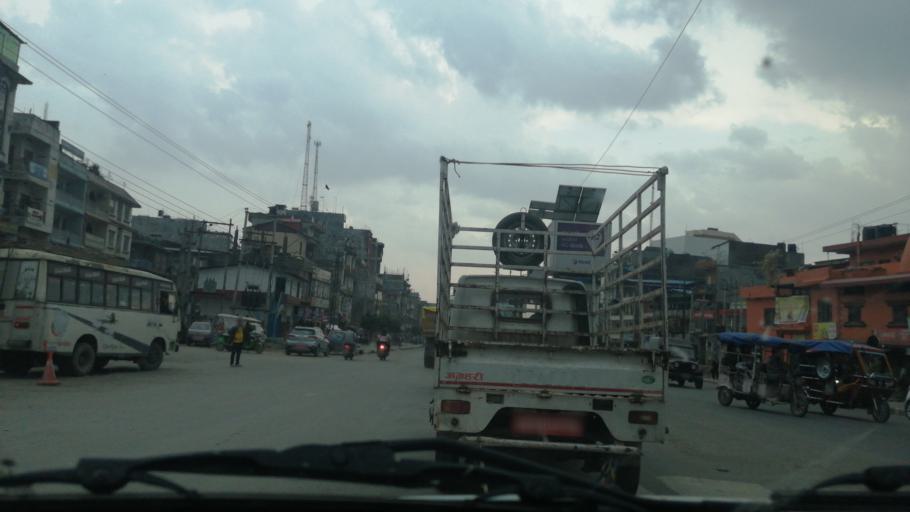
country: NP
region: Western Region
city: Butwal
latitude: 27.7010
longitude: 83.4661
